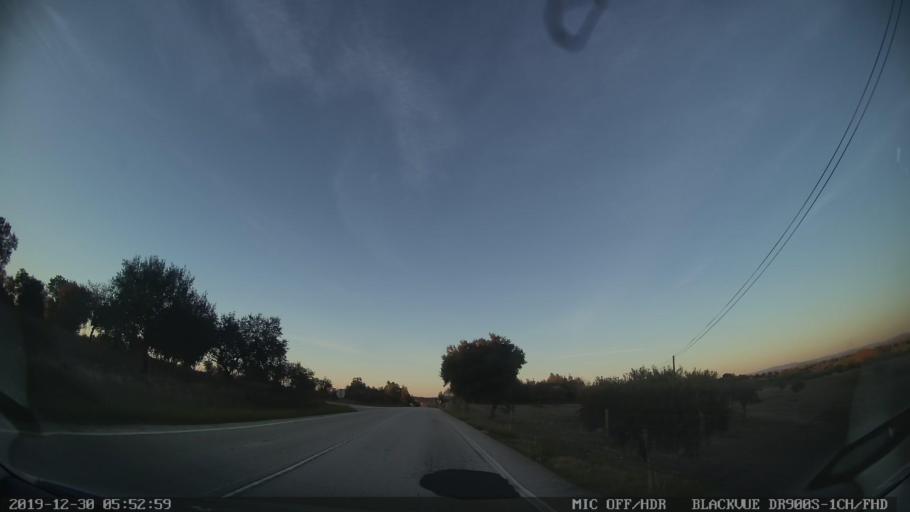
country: PT
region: Castelo Branco
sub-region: Idanha-A-Nova
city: Idanha-a-Nova
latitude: 40.0109
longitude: -7.2493
